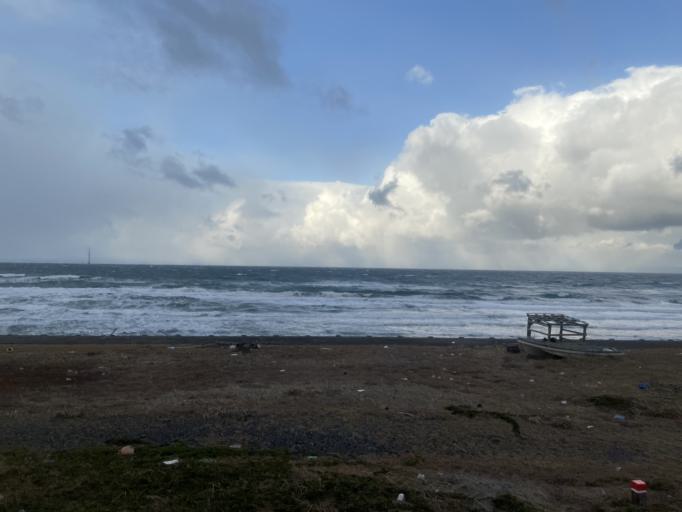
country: JP
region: Aomori
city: Mutsu
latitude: 40.9796
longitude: 141.2249
